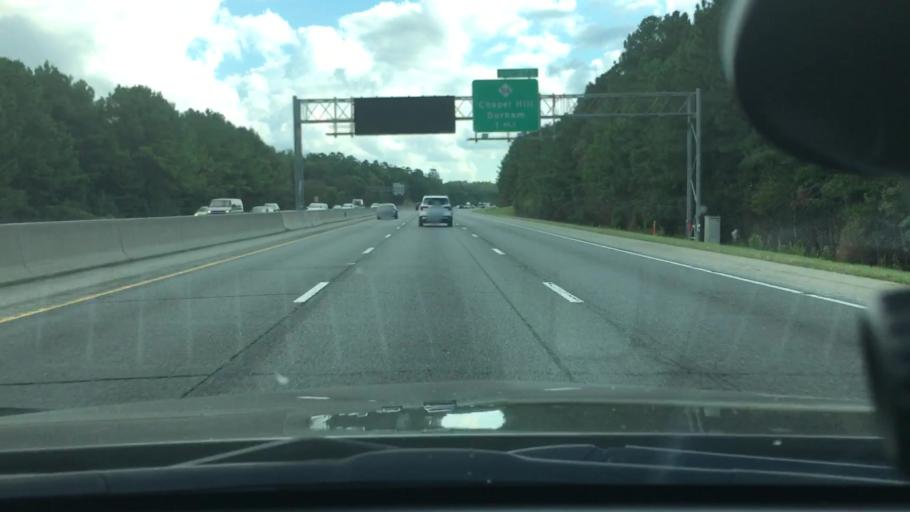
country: US
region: North Carolina
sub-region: Orange County
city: Chapel Hill
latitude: 35.9306
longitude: -78.9880
